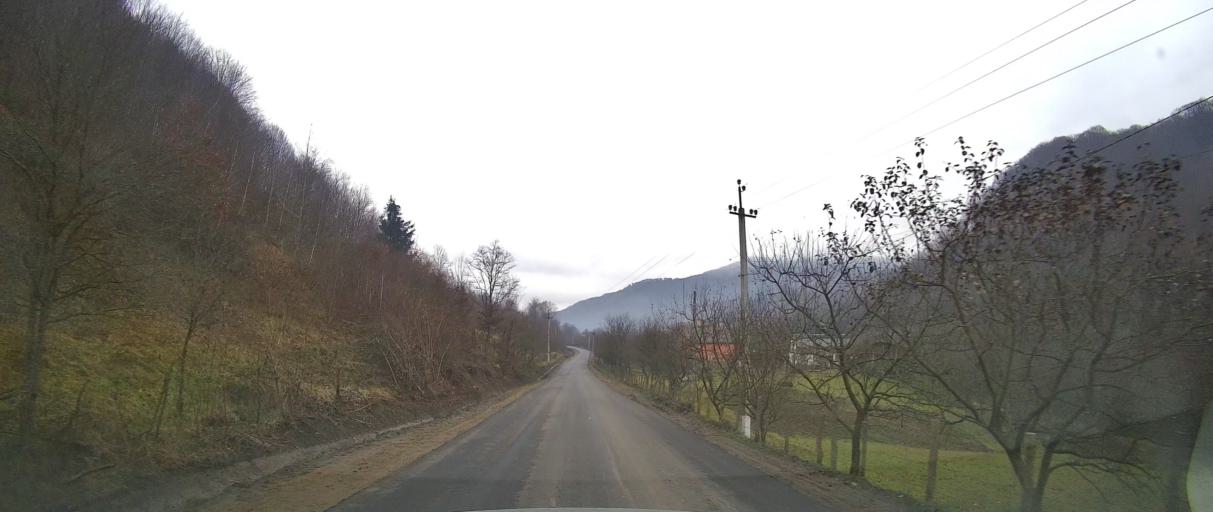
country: UA
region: Zakarpattia
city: Velykyi Bereznyi
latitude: 48.9583
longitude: 22.5474
